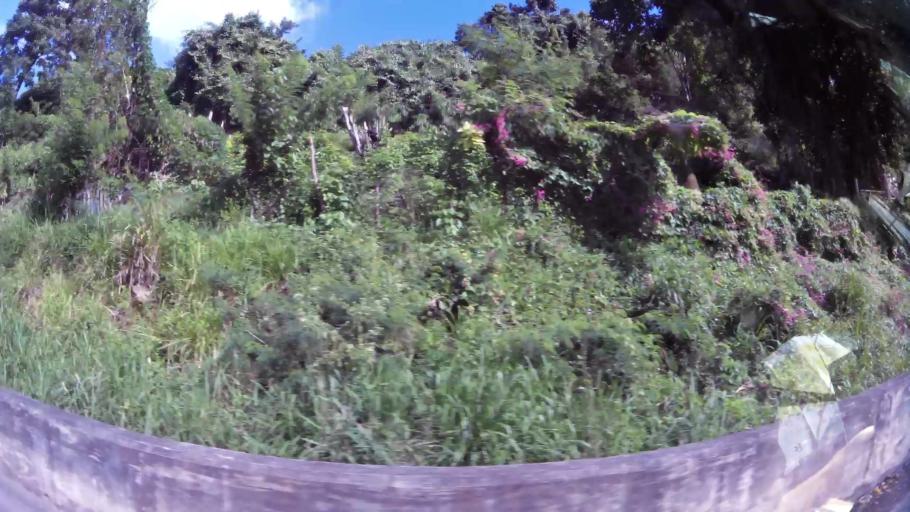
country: DM
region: Saint Luke
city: Pointe Michel
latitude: 15.2821
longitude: -61.3746
